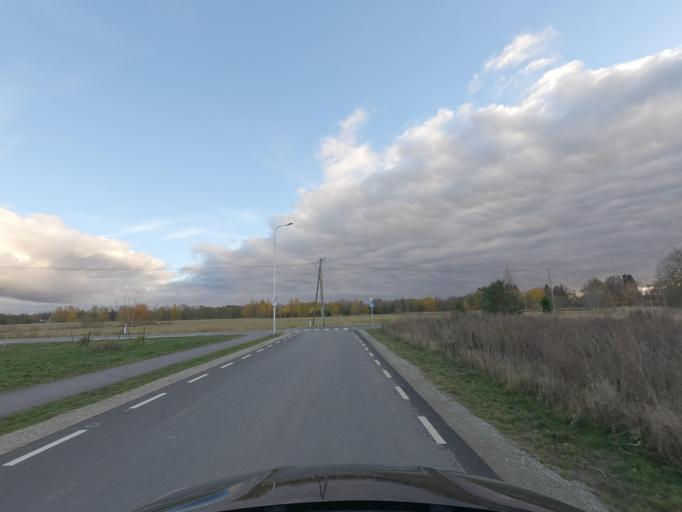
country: EE
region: Harju
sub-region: Saue vald
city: Laagri
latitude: 59.3609
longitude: 24.5731
